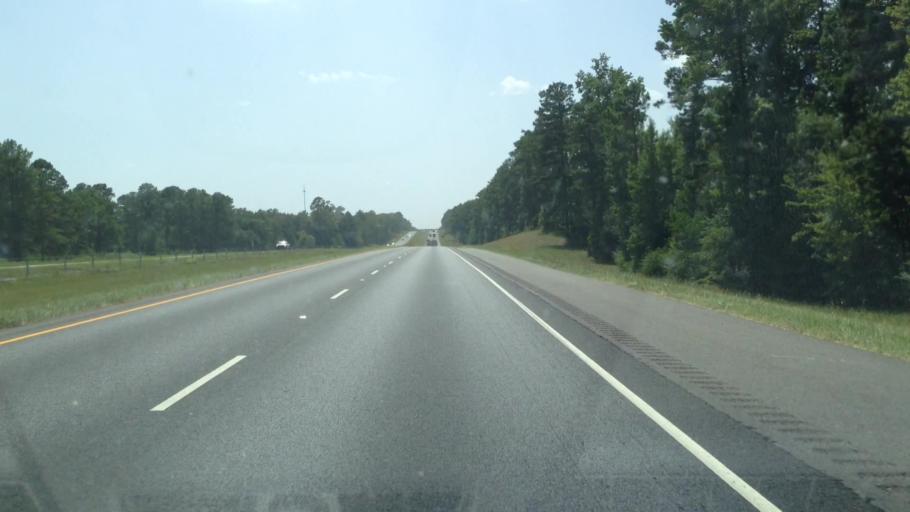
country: US
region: Louisiana
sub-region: Webster Parish
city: Minden
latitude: 32.5629
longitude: -93.1102
